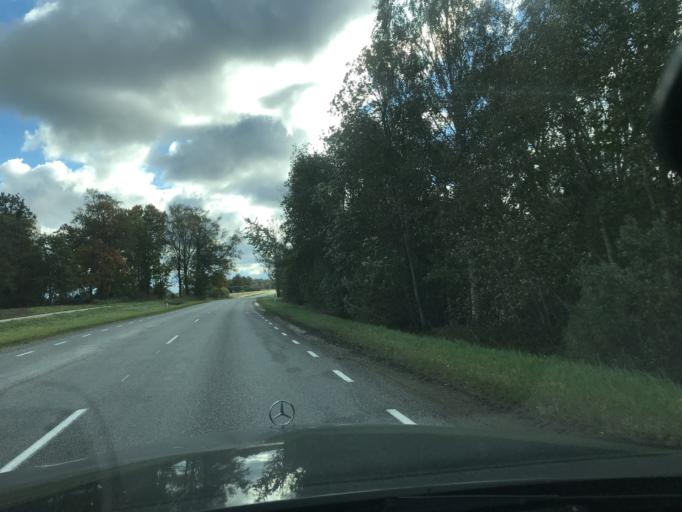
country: EE
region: Vorumaa
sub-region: Antsla vald
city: Vana-Antsla
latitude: 57.9410
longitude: 26.3071
